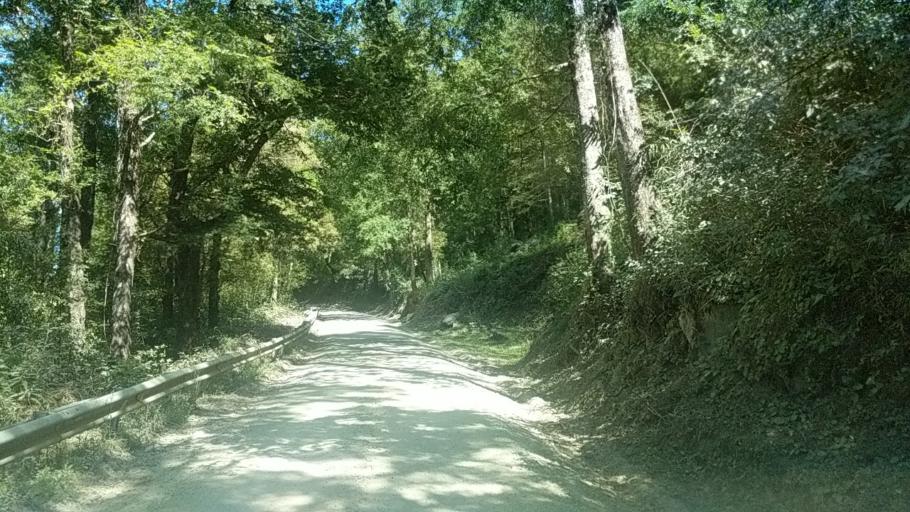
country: CL
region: Araucania
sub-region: Provincia de Cautin
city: Pucon
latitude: -39.0635
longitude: -71.7139
